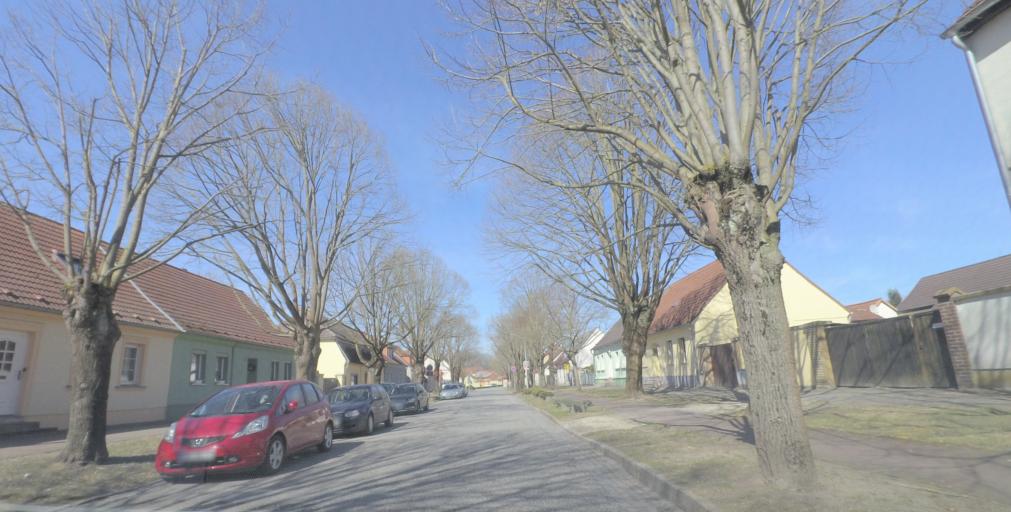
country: DE
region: Brandenburg
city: Neuruppin
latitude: 52.9477
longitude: 12.8485
